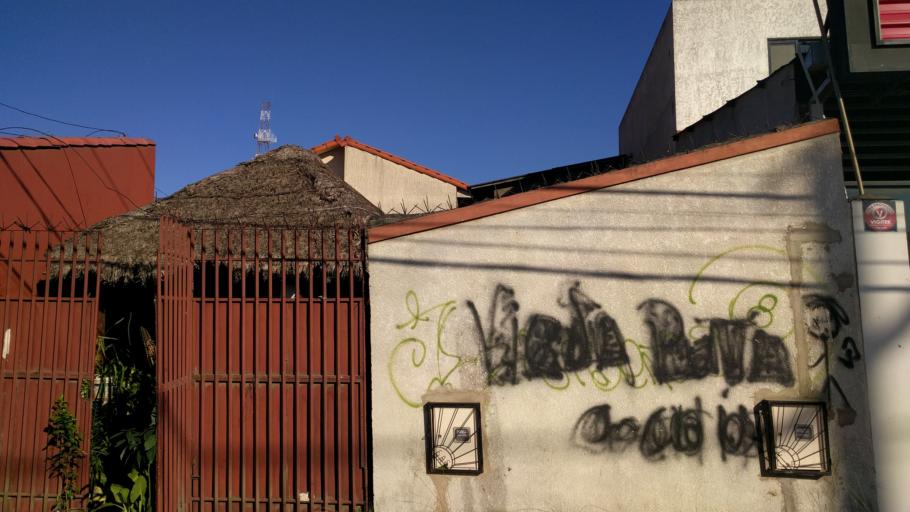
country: BO
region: Santa Cruz
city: Santa Cruz de la Sierra
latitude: -17.7536
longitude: -63.1954
